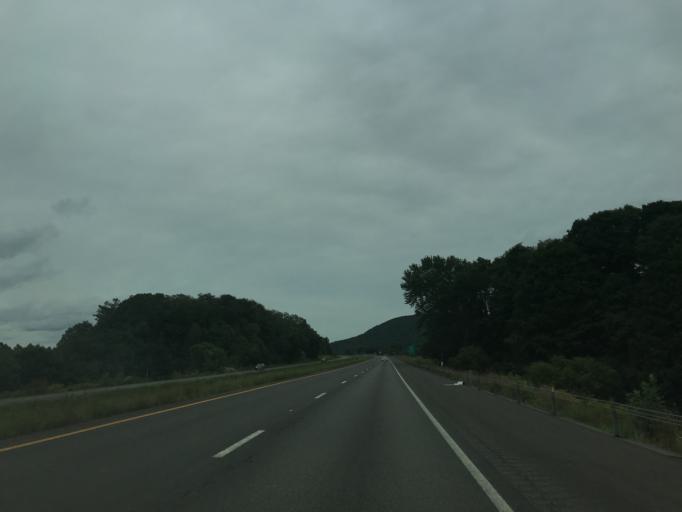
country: US
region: New York
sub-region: Otsego County
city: Unadilla
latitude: 42.3224
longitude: -75.3047
